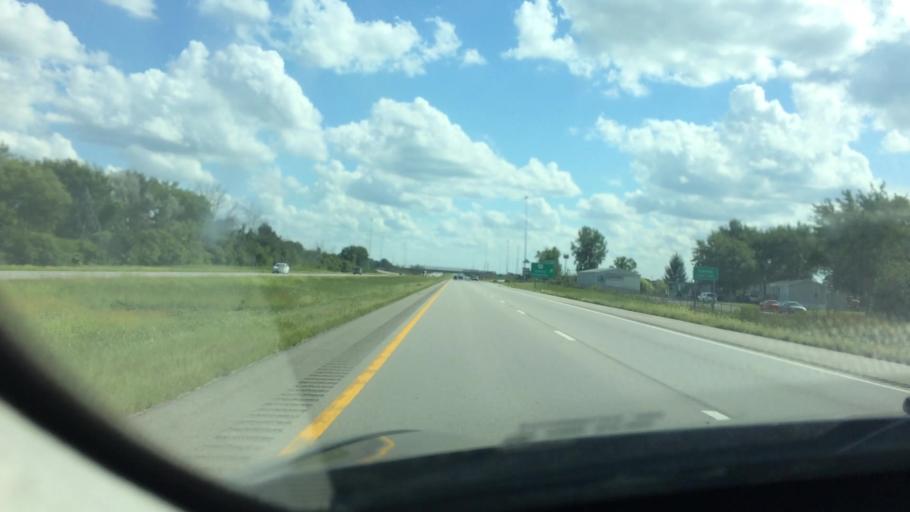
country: US
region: Ohio
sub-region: Shelby County
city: Sidney
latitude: 40.2956
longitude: -84.1815
